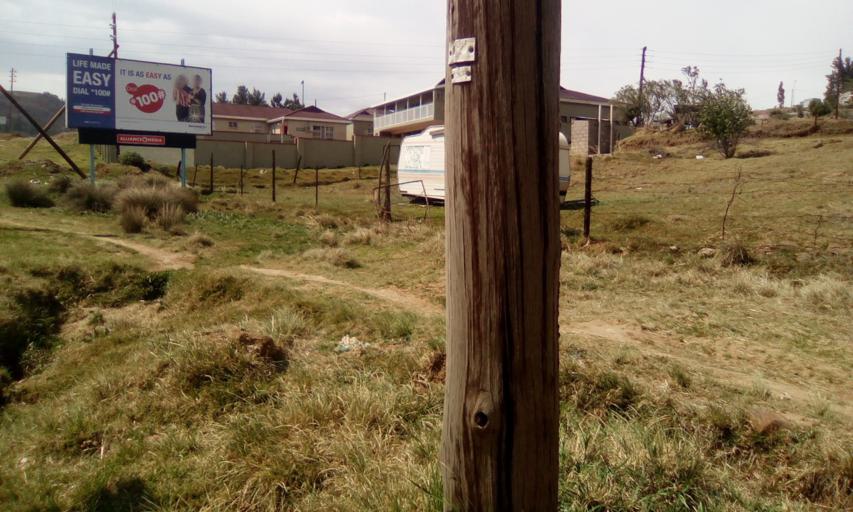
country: LS
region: Qacha's Nek
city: Qacha's Nek
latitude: -30.1147
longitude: 28.6805
